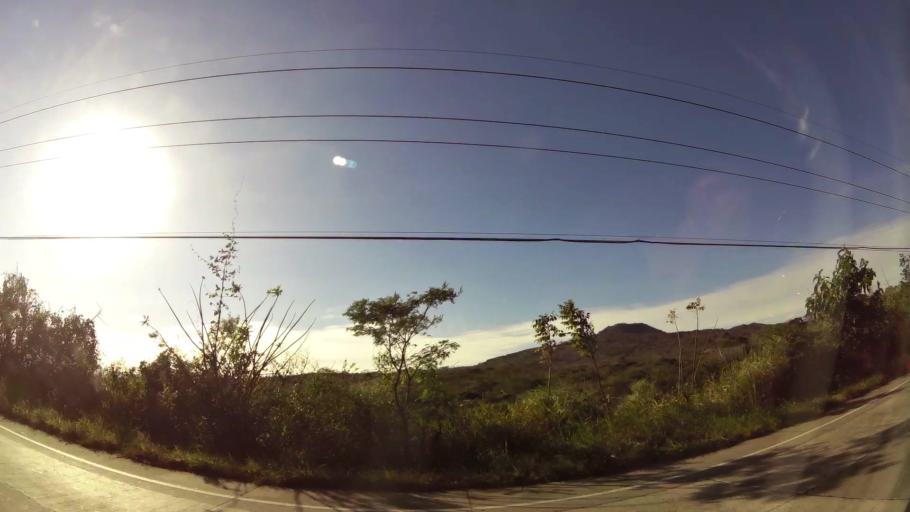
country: SV
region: Santa Ana
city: Metapan
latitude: 14.2576
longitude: -89.4610
